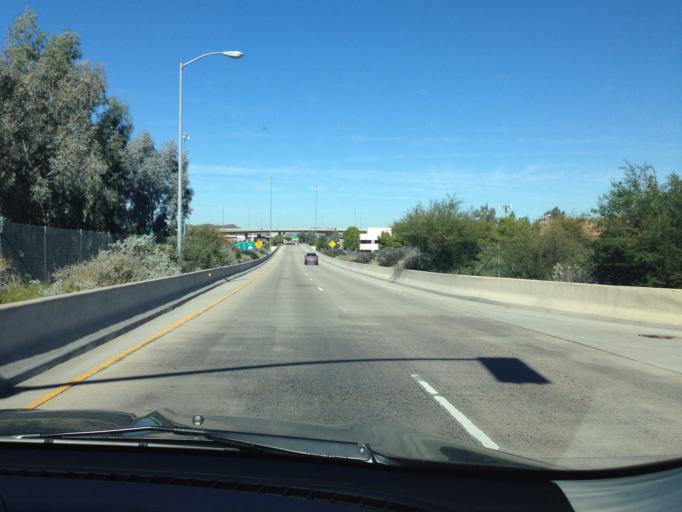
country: US
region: Arizona
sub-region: Maricopa County
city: Glendale
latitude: 33.6620
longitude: -112.1133
